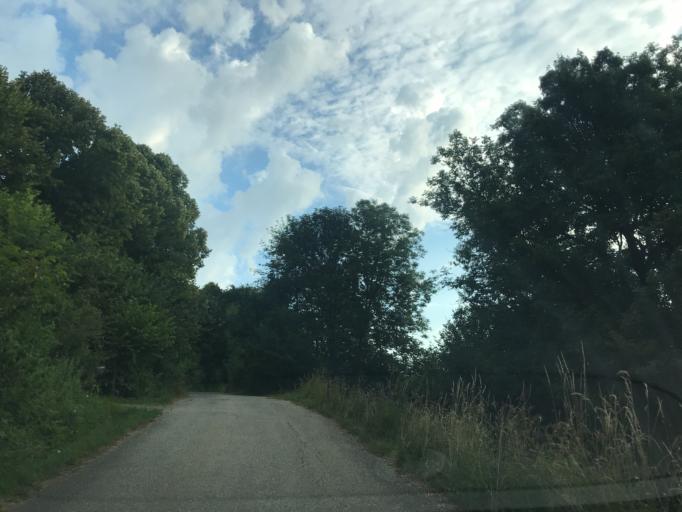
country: FR
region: Rhone-Alpes
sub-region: Departement de l'Isere
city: Saint-Vincent-de-Mercuze
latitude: 45.4096
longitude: 5.9453
